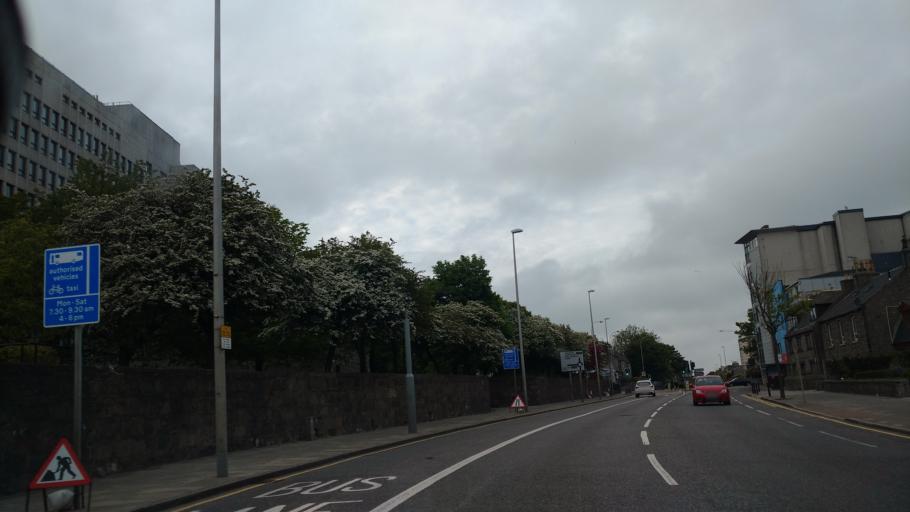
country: GB
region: Scotland
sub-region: Aberdeen City
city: Aberdeen
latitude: 57.1655
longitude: -2.0975
